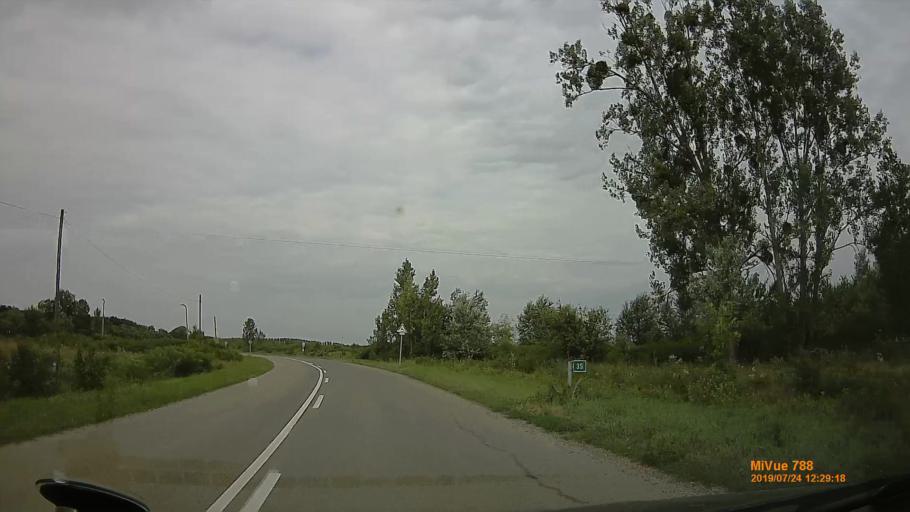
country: HU
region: Szabolcs-Szatmar-Bereg
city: Vasarosnameny
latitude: 48.1498
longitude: 22.3483
